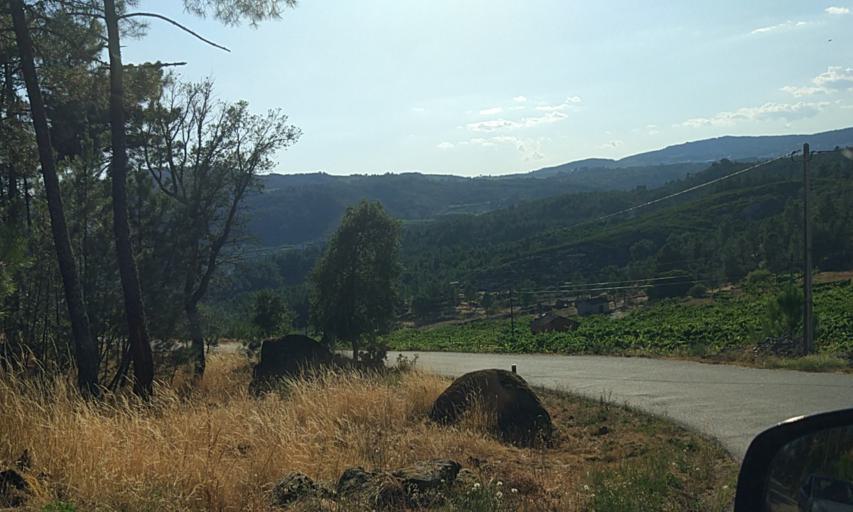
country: PT
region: Viseu
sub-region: Sao Joao da Pesqueira
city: Sao Joao da Pesqueira
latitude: 41.2548
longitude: -7.4203
